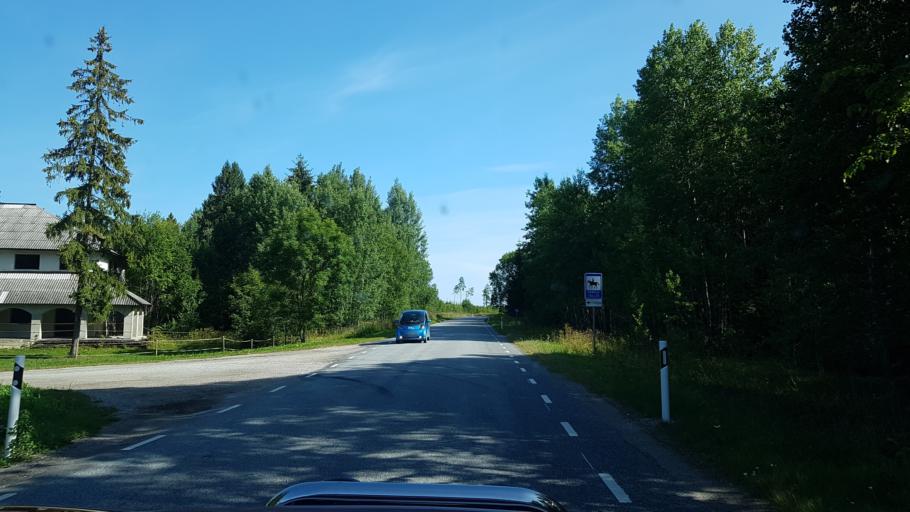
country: EE
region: Harju
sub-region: Raasiku vald
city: Raasiku
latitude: 59.2856
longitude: 25.1620
